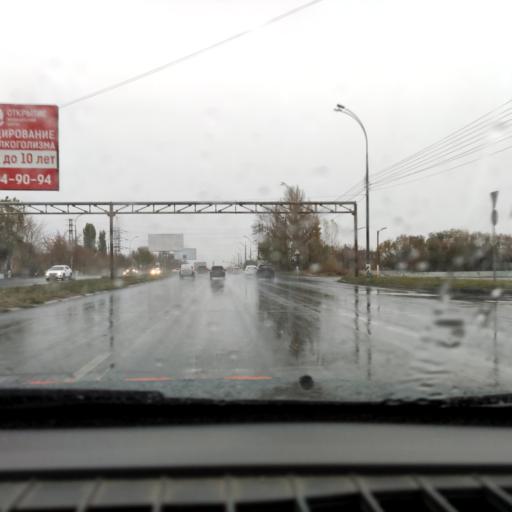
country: RU
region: Samara
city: Tol'yatti
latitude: 53.5437
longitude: 49.2854
